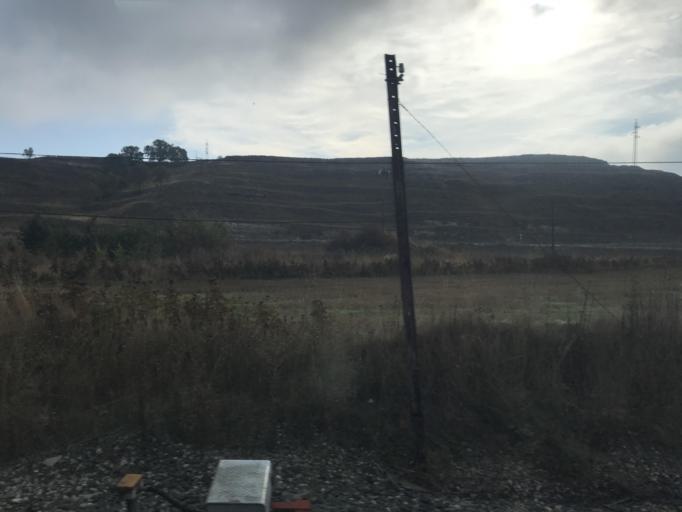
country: ES
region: Castille and Leon
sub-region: Provincia de Burgos
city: Briviesca
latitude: 42.5382
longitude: -3.3197
